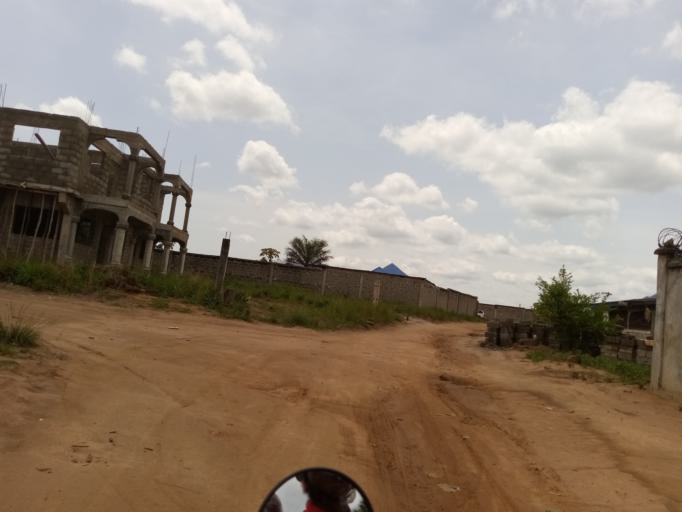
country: SL
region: Western Area
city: Waterloo
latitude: 8.3304
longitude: -13.0321
